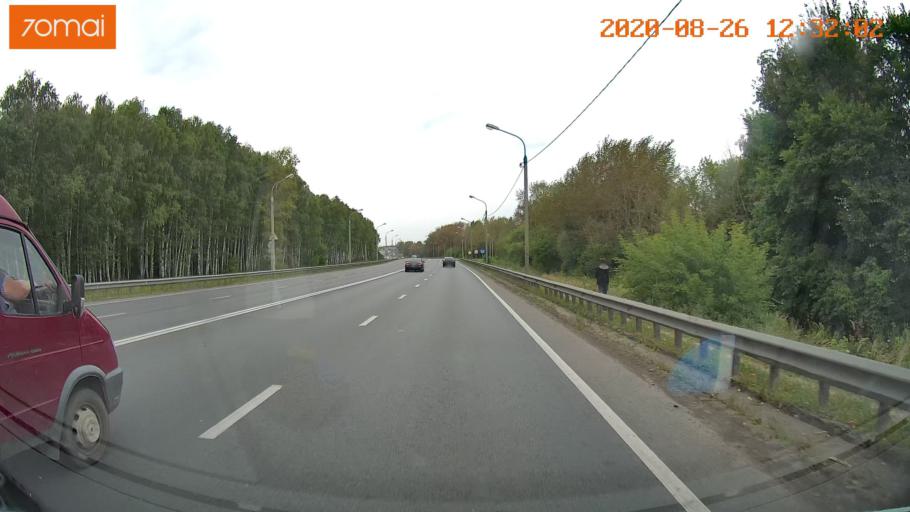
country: RU
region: Rjazan
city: Ryazan'
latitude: 54.5748
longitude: 39.7973
